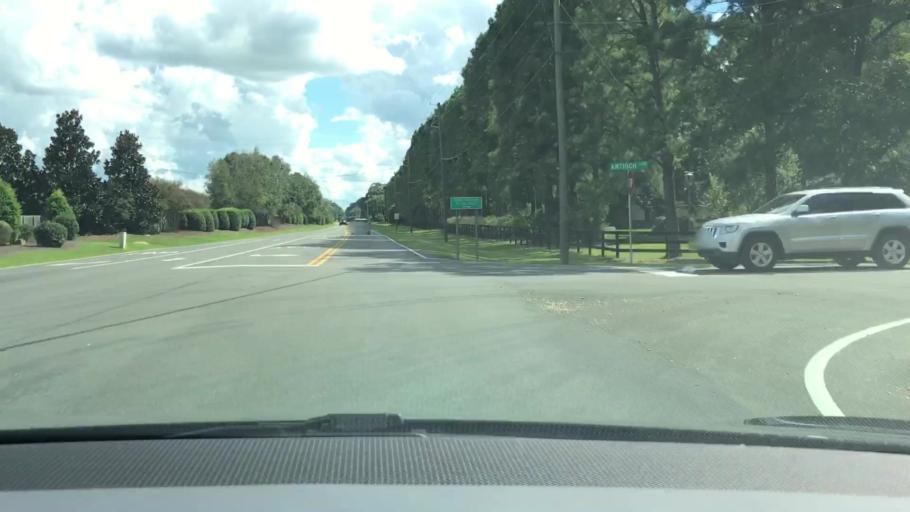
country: US
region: Alabama
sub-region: Montgomery County
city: Pike Road
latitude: 32.3542
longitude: -86.0950
